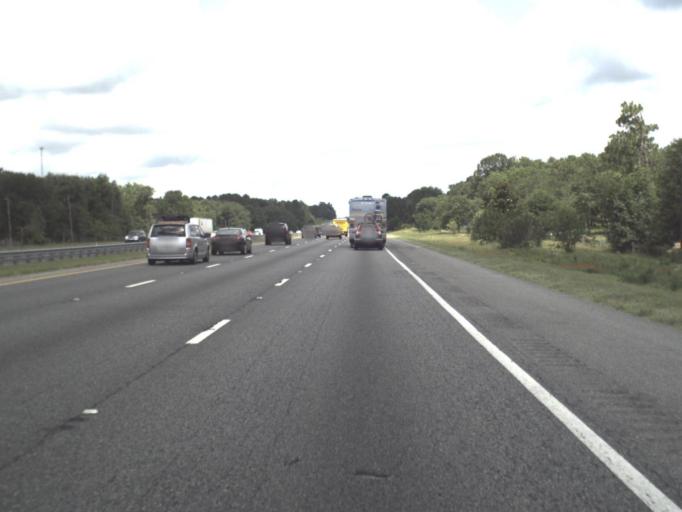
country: US
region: Florida
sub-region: Columbia County
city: Five Points
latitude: 30.2220
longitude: -82.7133
